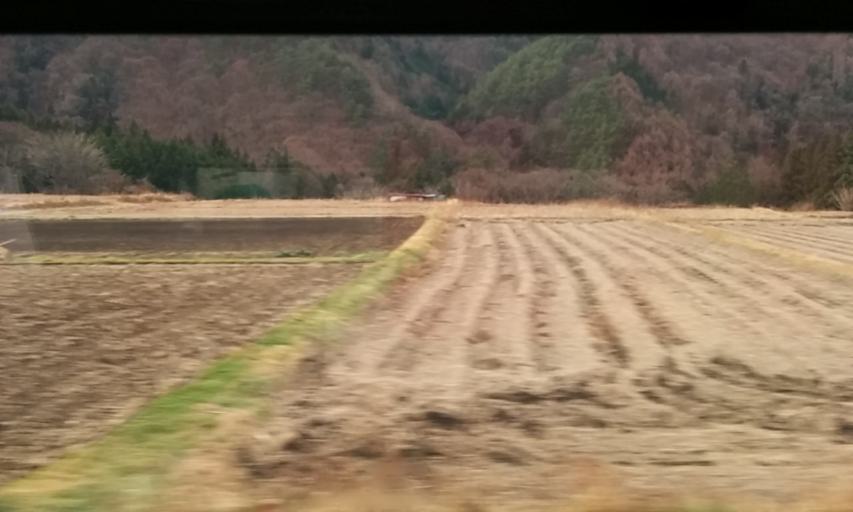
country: JP
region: Nagano
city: Shiojiri
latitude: 36.0652
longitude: 137.9010
